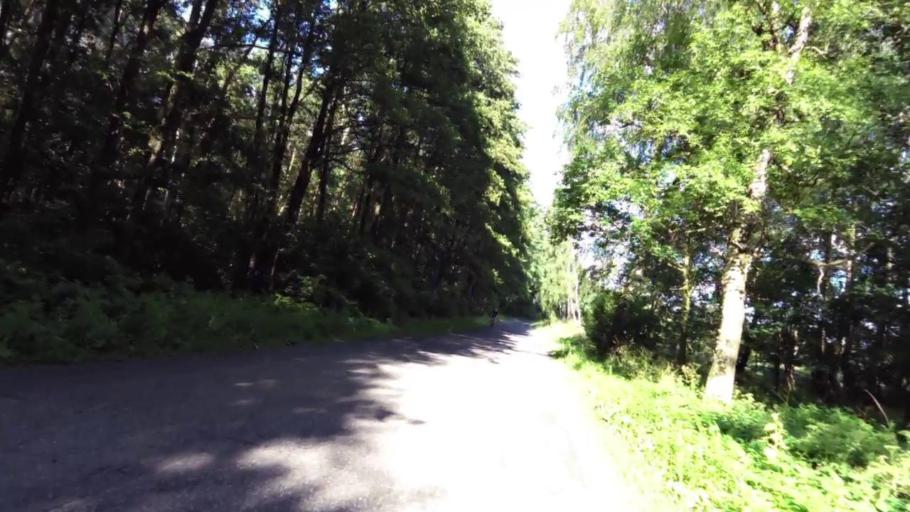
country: PL
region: West Pomeranian Voivodeship
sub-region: Powiat slawienski
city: Slawno
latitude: 54.4366
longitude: 16.7546
